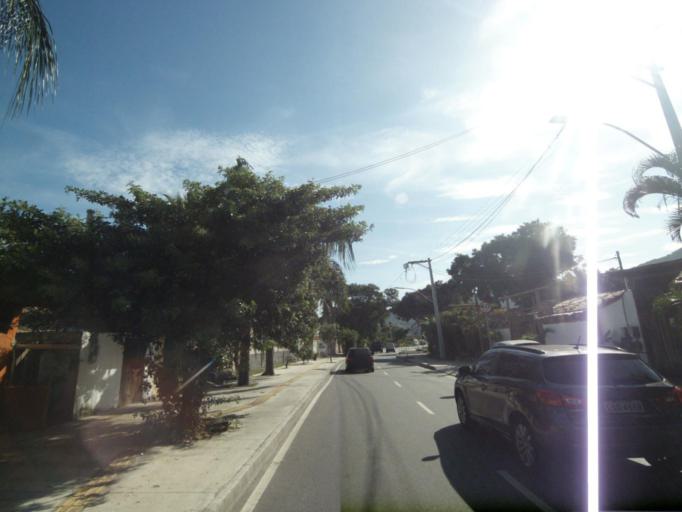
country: BR
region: Rio de Janeiro
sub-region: Niteroi
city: Niteroi
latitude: -22.9347
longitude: -43.0705
